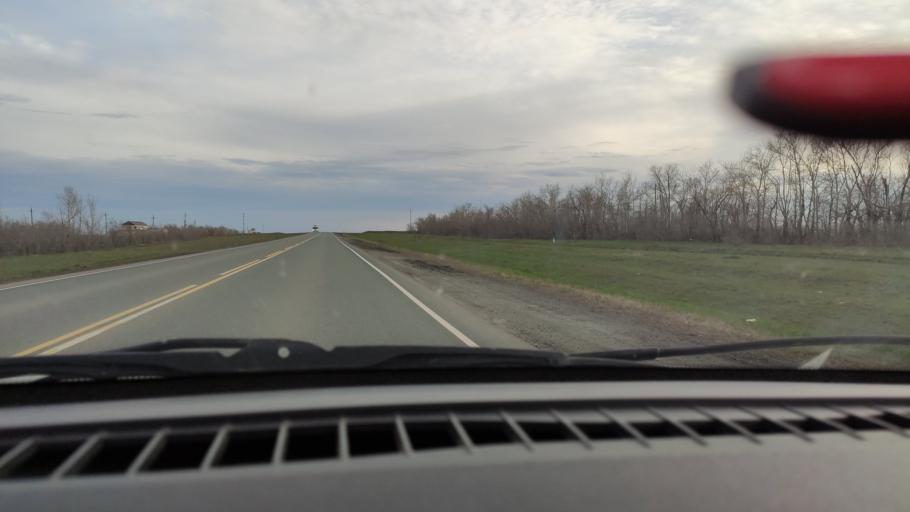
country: RU
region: Orenburg
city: Sakmara
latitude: 52.0611
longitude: 55.2586
